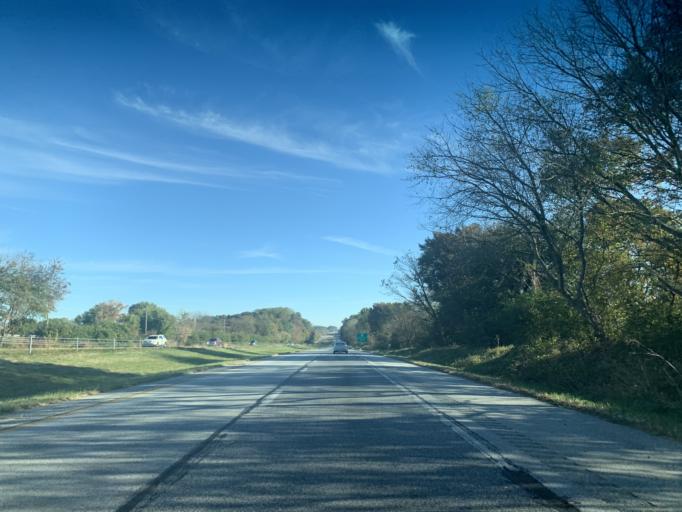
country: US
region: Pennsylvania
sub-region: Chester County
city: Oxford
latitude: 39.7710
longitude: -76.0104
